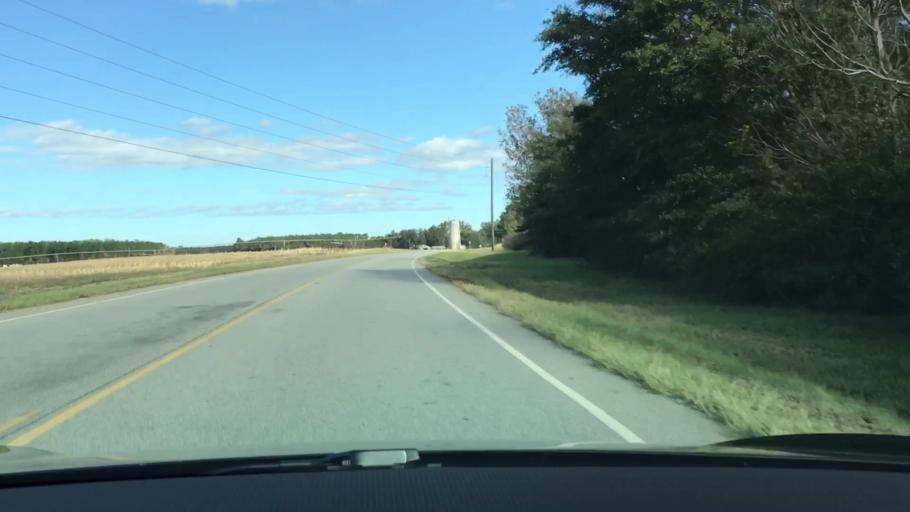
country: US
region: Georgia
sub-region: Jefferson County
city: Wrens
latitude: 33.1499
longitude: -82.4573
